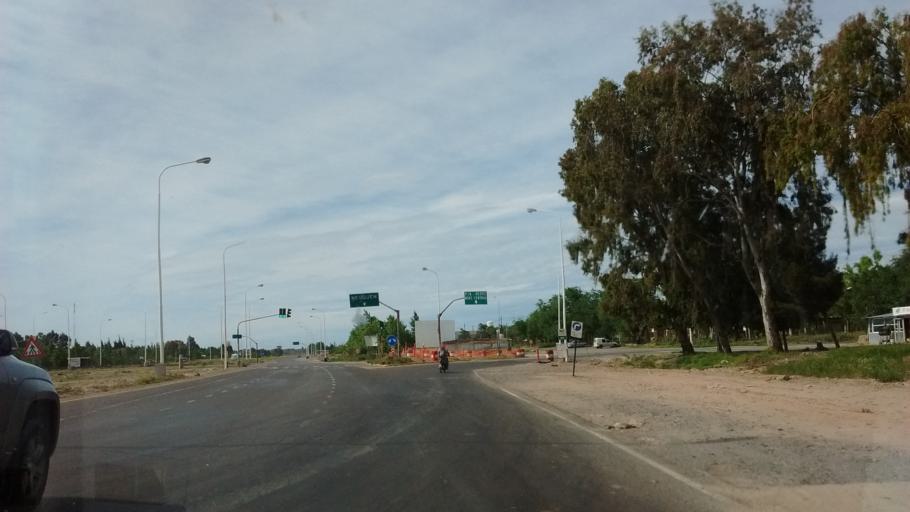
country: AR
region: Neuquen
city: Neuquen
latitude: -38.8976
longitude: -68.0890
